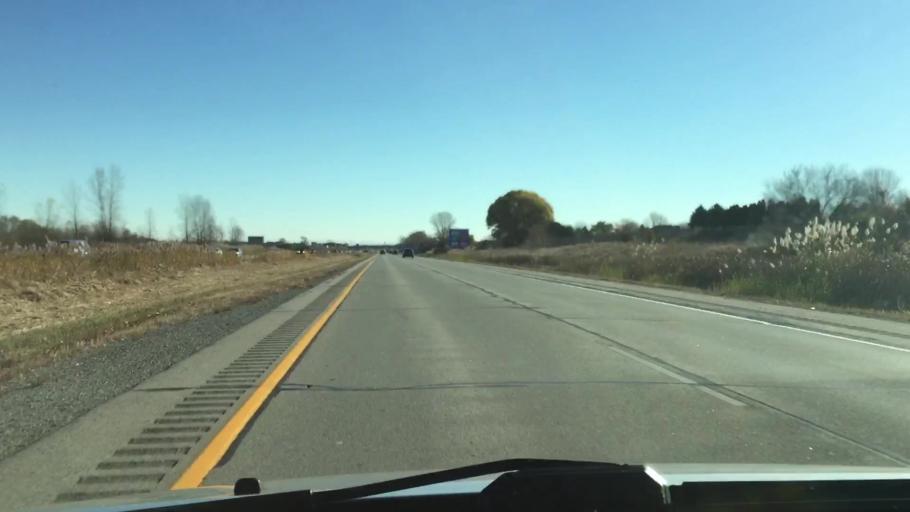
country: US
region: Wisconsin
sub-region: Outagamie County
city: Appleton
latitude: 44.2983
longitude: -88.3945
